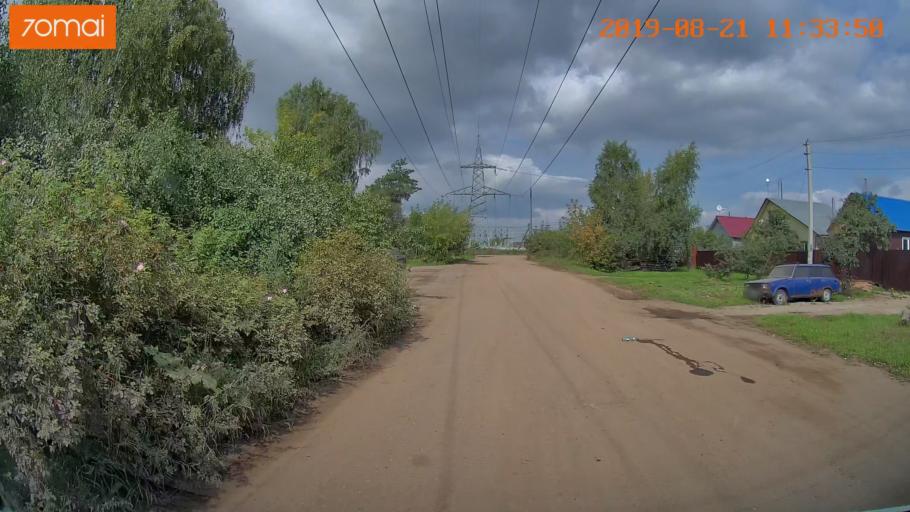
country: RU
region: Ivanovo
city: Novo-Talitsy
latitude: 56.9864
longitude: 40.9110
